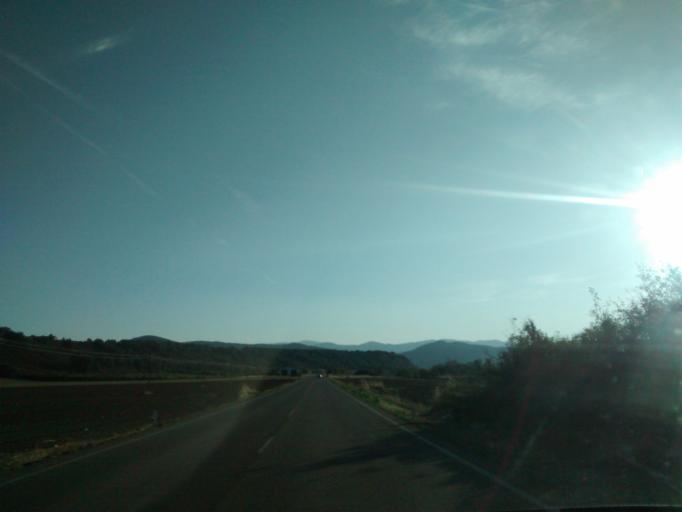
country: ES
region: Aragon
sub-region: Provincia de Huesca
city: Santa Cruz de la Seros
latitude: 42.5843
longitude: -0.7401
